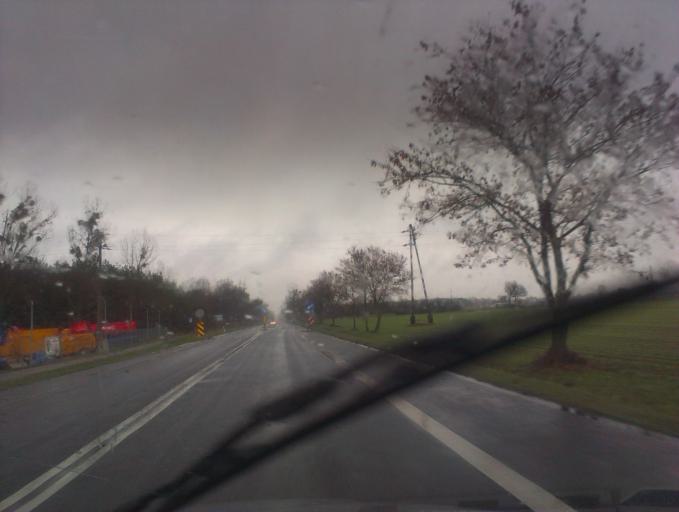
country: PL
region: Greater Poland Voivodeship
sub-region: Powiat obornicki
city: Oborniki
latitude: 52.6676
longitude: 16.8471
